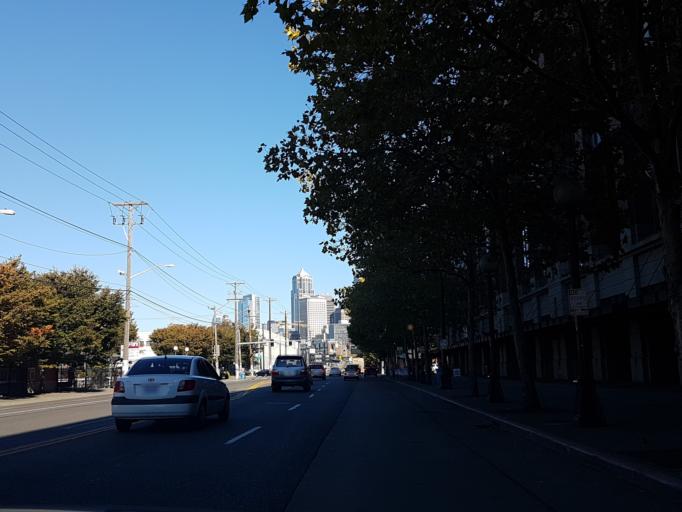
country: US
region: Washington
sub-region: King County
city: Seattle
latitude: 47.5911
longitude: -122.3341
